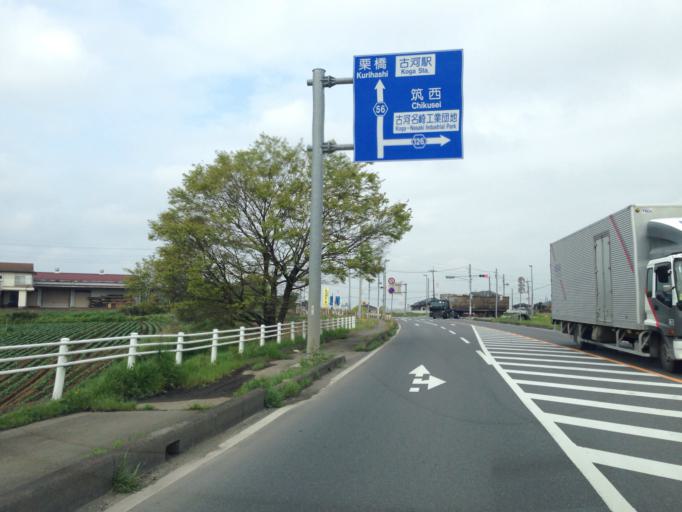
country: JP
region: Ibaraki
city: Sakai
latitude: 36.1708
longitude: 139.8426
